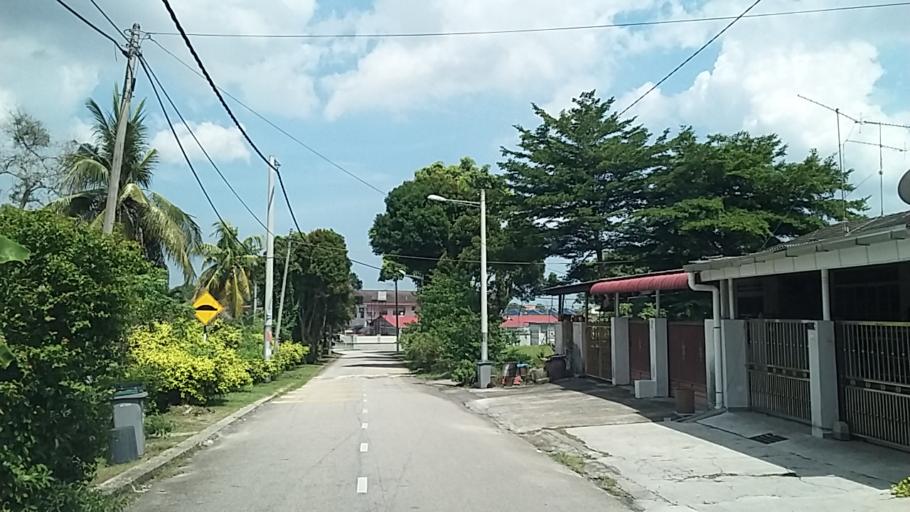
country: MY
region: Johor
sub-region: Daerah Batu Pahat
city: Batu Pahat
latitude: 1.8425
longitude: 102.9454
